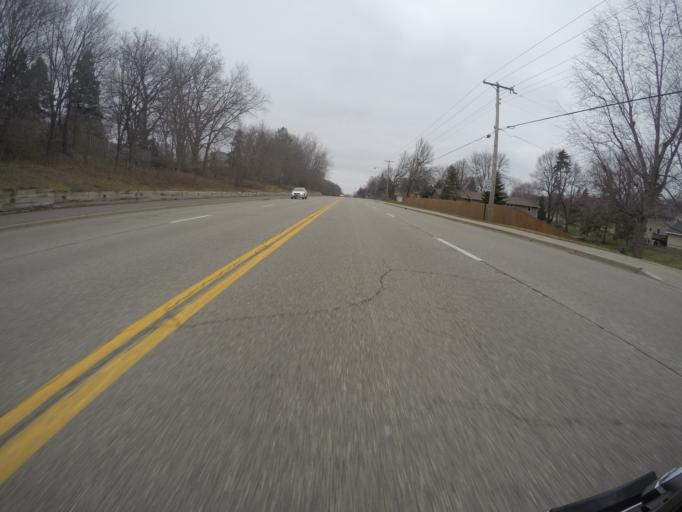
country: US
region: Minnesota
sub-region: Hennepin County
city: Eden Prairie
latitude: 44.8794
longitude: -93.4499
